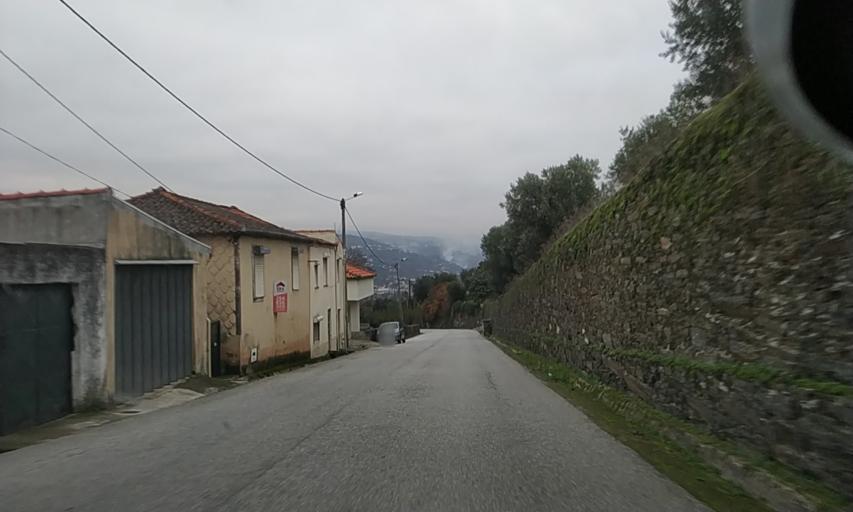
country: PT
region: Vila Real
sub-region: Peso da Regua
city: Peso da Regua
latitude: 41.1479
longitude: -7.7922
